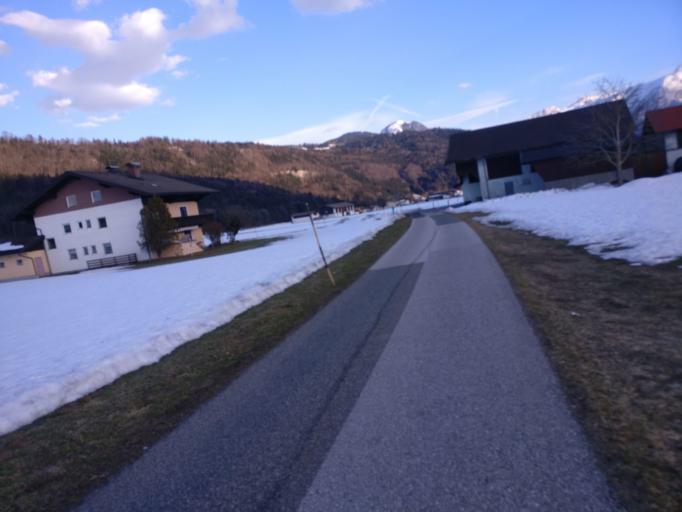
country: AT
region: Salzburg
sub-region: Politischer Bezirk Hallein
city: Kuchl
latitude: 47.6495
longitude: 13.1534
